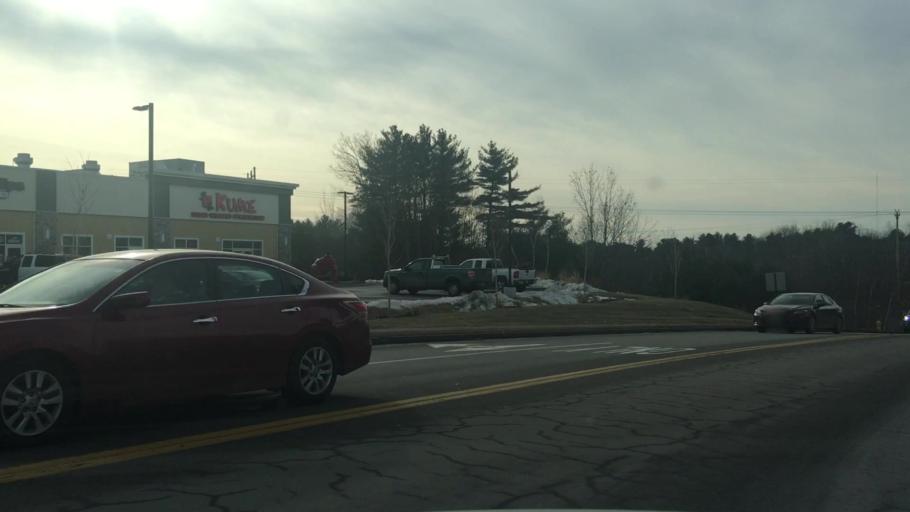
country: US
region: Maine
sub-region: Sagadahoc County
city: Topsham
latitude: 43.9365
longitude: -69.9811
